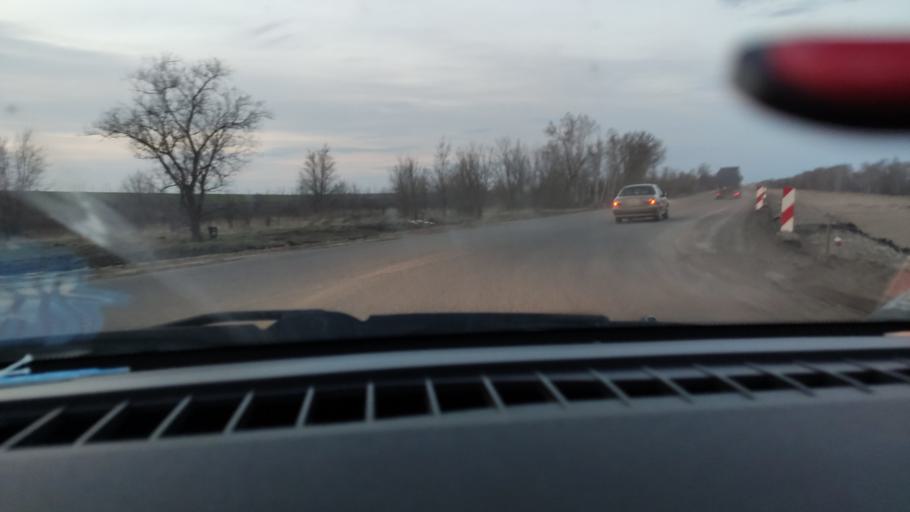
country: RU
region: Saratov
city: Sinodskoye
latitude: 52.0217
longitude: 46.7069
